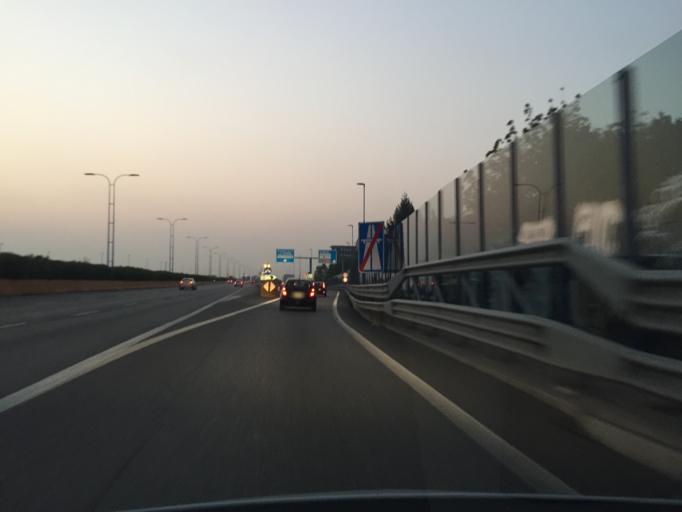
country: IT
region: Lombardy
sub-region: Provincia di Brescia
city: Roncadelle
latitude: 45.5238
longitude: 10.1802
